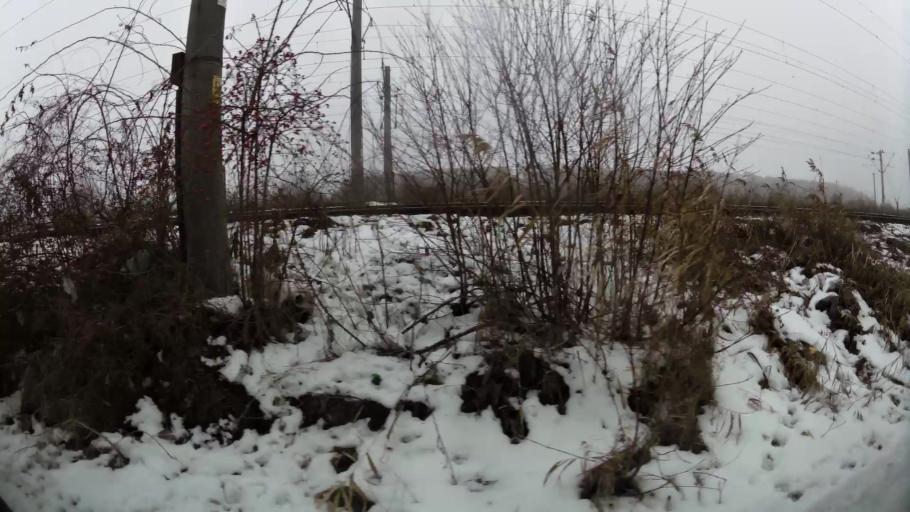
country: RO
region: Ilfov
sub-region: Comuna Chitila
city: Rudeni
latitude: 44.4696
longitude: 25.9792
